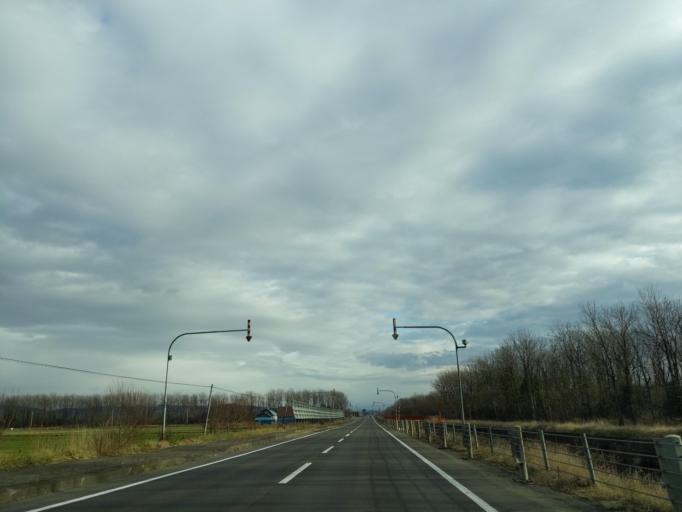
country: JP
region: Hokkaido
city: Kitahiroshima
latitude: 42.9707
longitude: 141.6611
